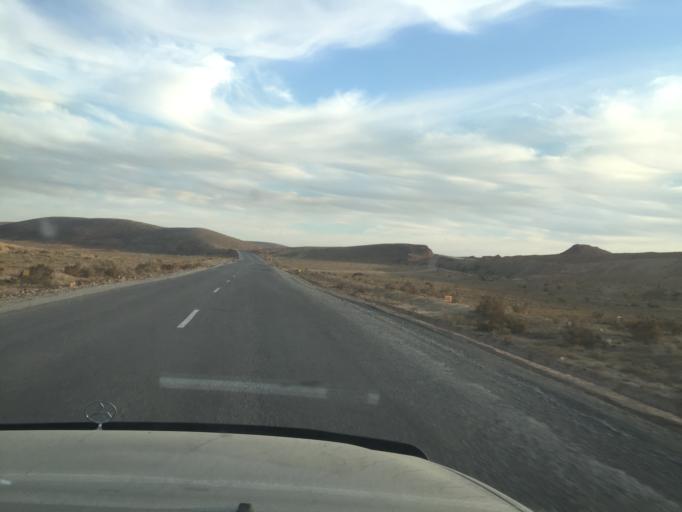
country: KZ
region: Almaty Oblysy
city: Ulken
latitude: 45.0653
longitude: 73.9999
